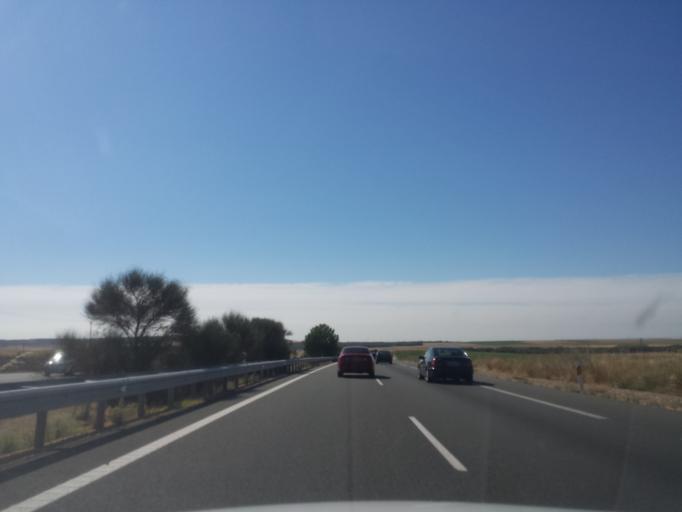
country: ES
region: Castille and Leon
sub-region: Provincia de Valladolid
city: Vega de Valdetronco
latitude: 41.5697
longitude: -5.0916
